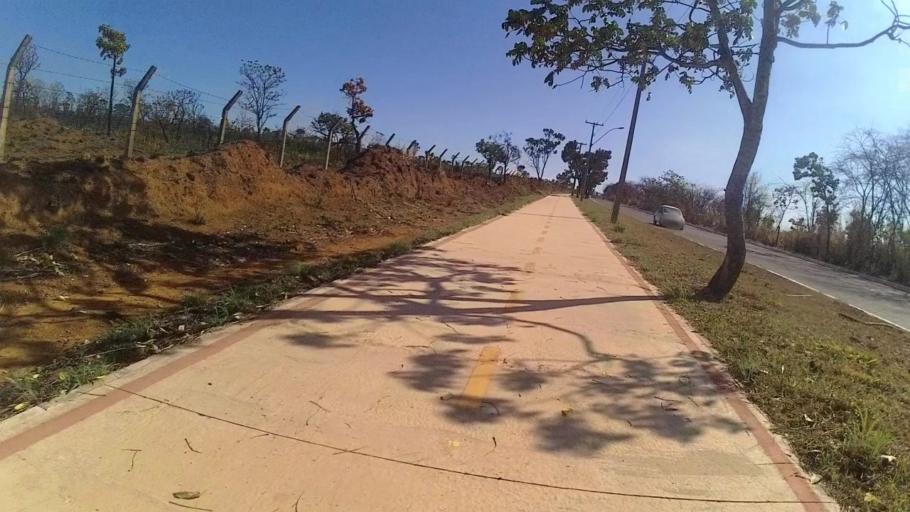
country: BR
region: Federal District
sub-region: Brasilia
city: Brasilia
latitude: -15.6535
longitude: -47.8947
